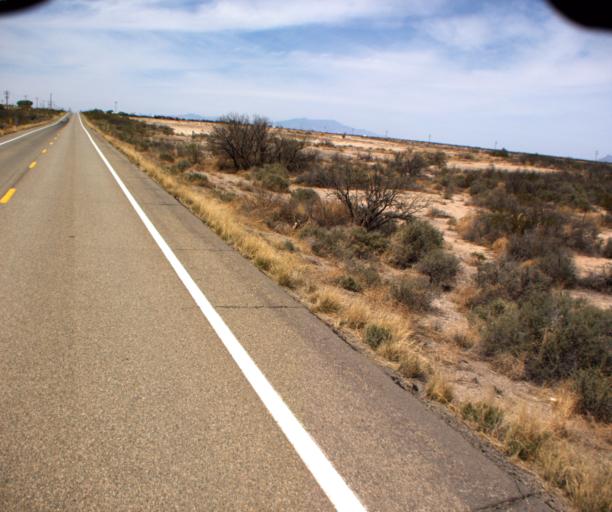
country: US
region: New Mexico
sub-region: Hidalgo County
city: Lordsburg
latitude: 32.2624
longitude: -109.2090
